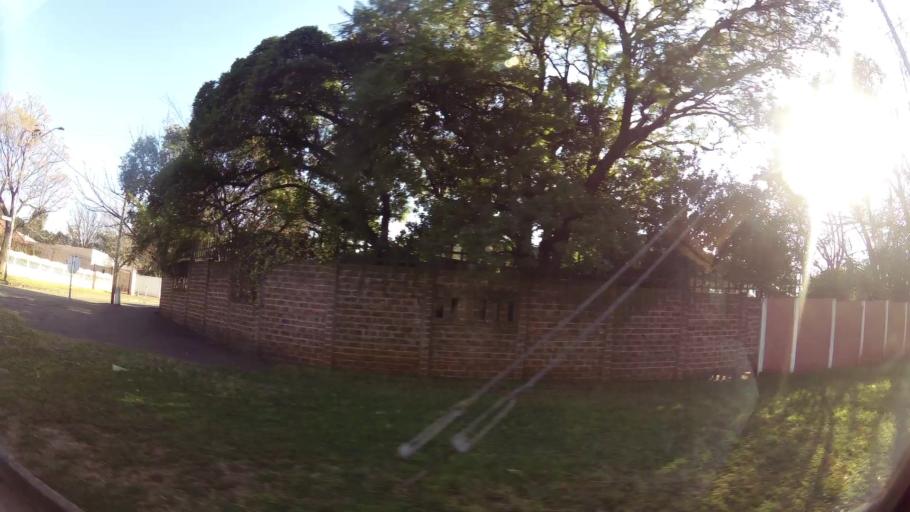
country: ZA
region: Gauteng
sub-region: Ekurhuleni Metropolitan Municipality
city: Germiston
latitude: -26.2006
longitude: 28.1299
